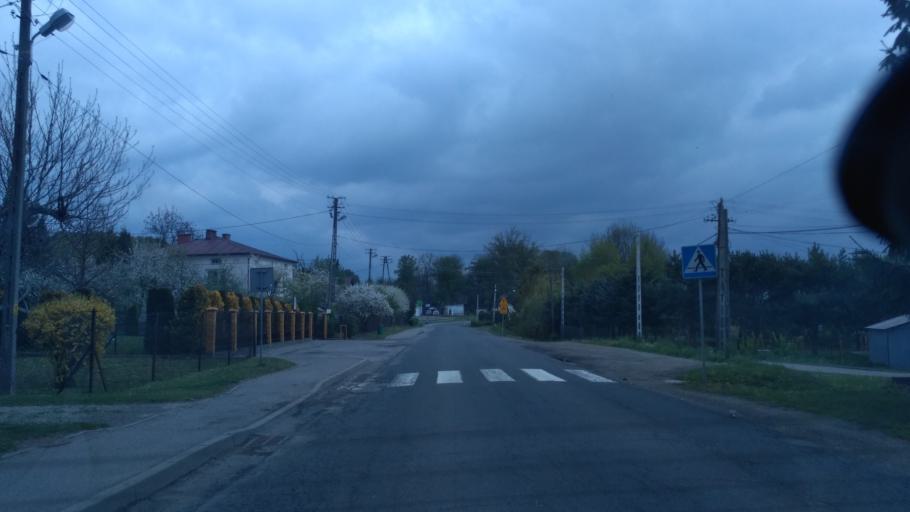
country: PL
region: Subcarpathian Voivodeship
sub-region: Powiat brzozowski
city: Jasionow
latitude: 49.6450
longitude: 21.9426
